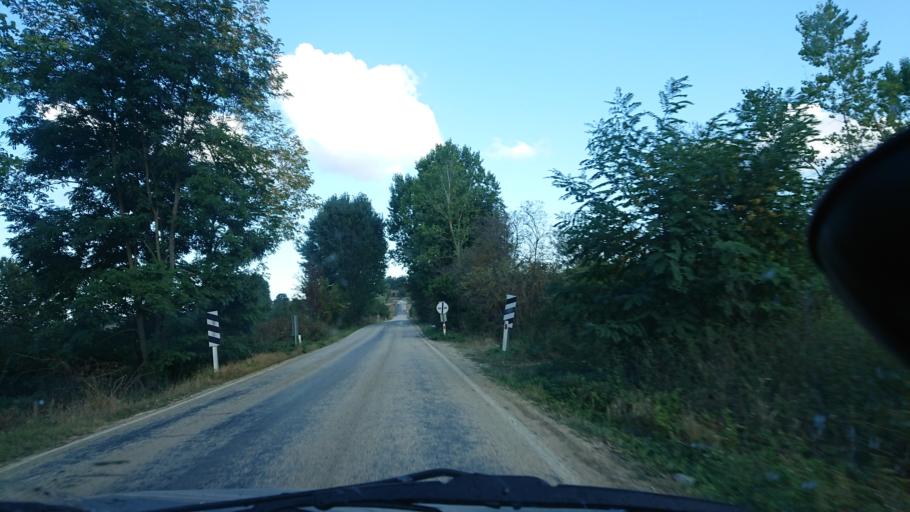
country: TR
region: Bilecik
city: Pazaryeri
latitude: 40.0098
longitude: 29.8616
